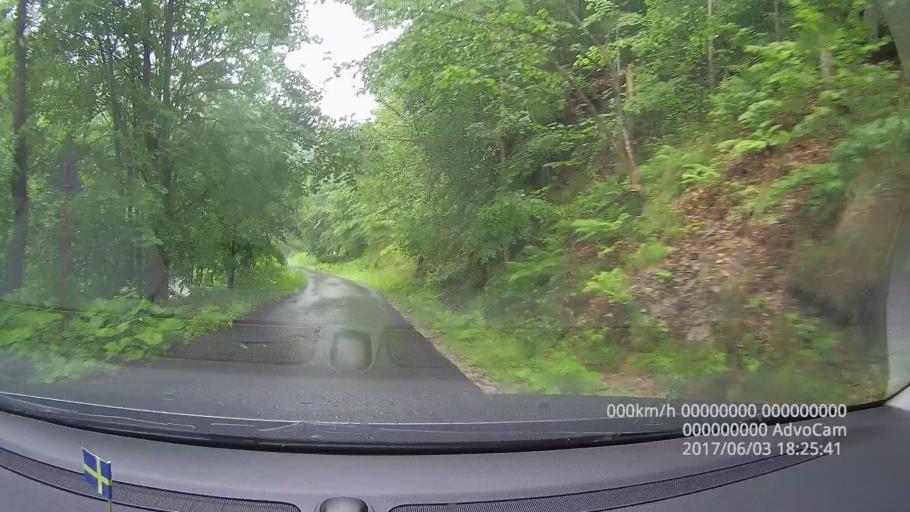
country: RO
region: Gorj
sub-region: Comuna Runcu
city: Dobrita
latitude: 45.1736
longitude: 23.1915
